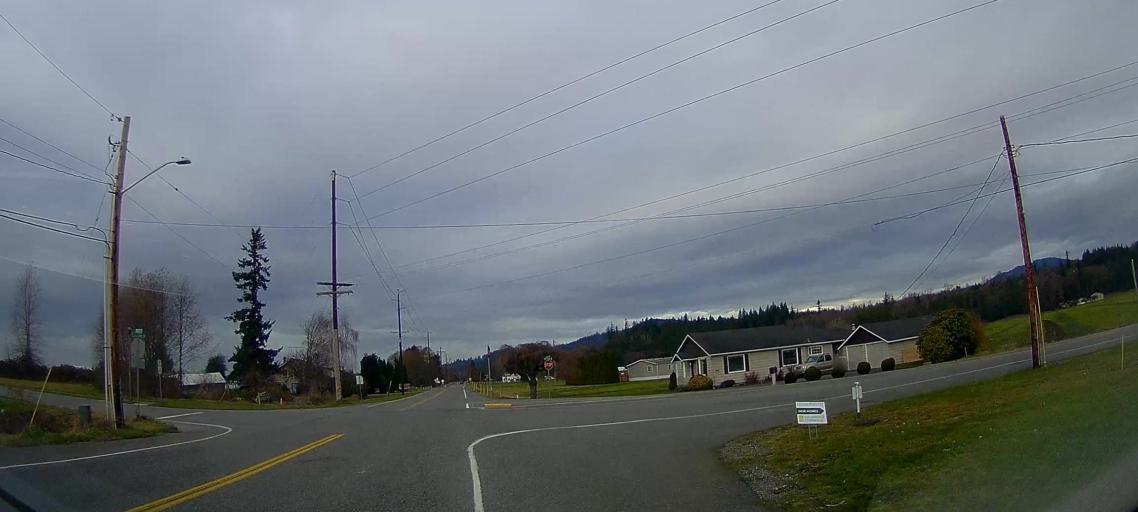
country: US
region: Washington
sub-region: Skagit County
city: Sedro-Woolley
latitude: 48.5146
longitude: -122.2542
